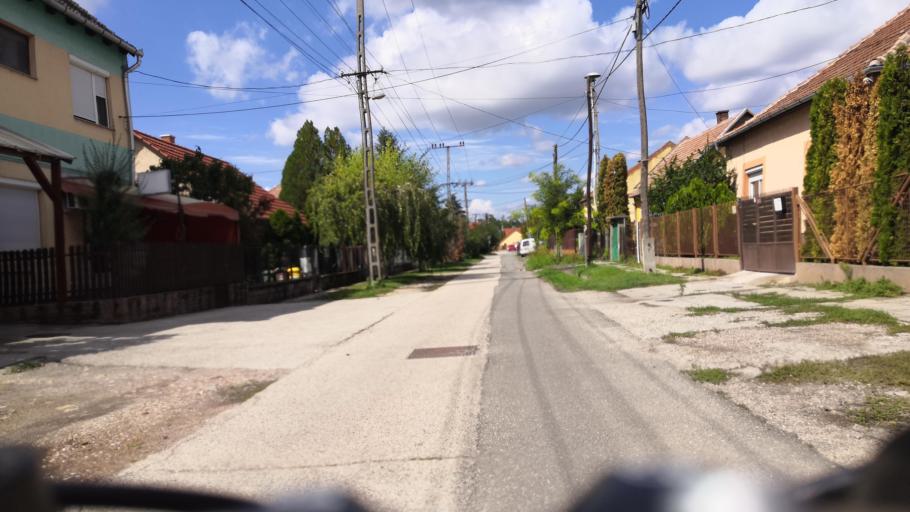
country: HU
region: Csongrad
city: Szeged
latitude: 46.2770
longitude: 20.1223
